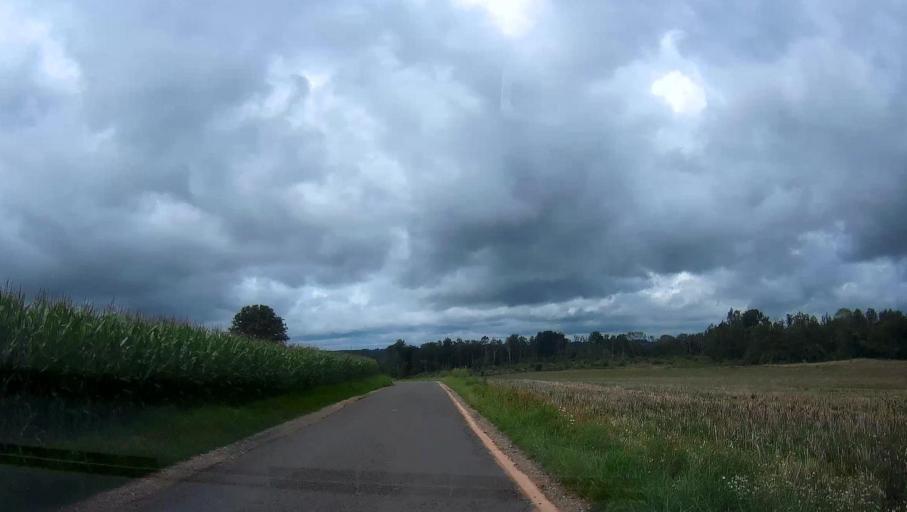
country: FR
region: Champagne-Ardenne
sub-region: Departement des Ardennes
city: Tournes
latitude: 49.7489
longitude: 4.5763
